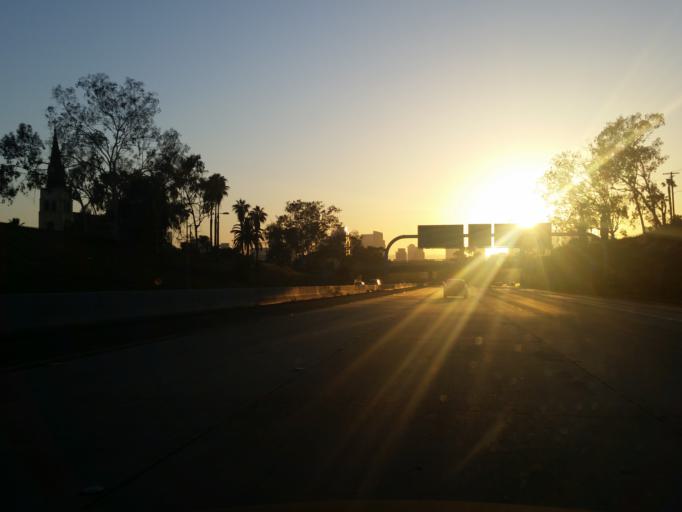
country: US
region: California
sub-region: San Diego County
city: San Diego
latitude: 32.7134
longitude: -117.1411
